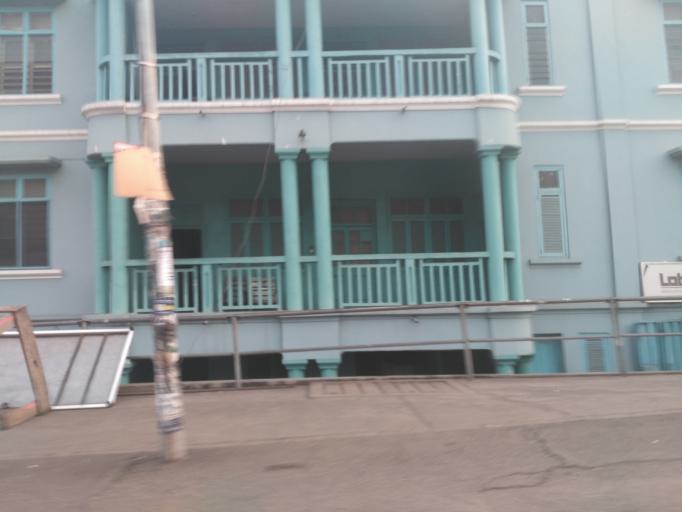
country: GH
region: Ashanti
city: Kumasi
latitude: 6.6897
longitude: -1.6084
